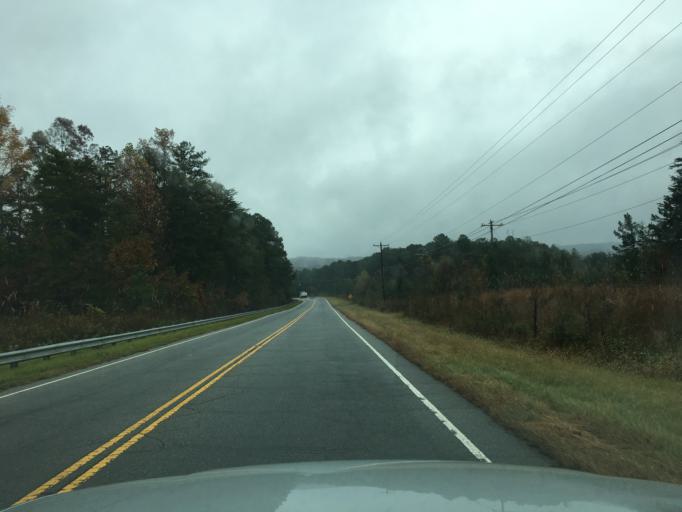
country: US
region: South Carolina
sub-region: Oconee County
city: Utica
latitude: 34.7870
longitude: -82.8965
